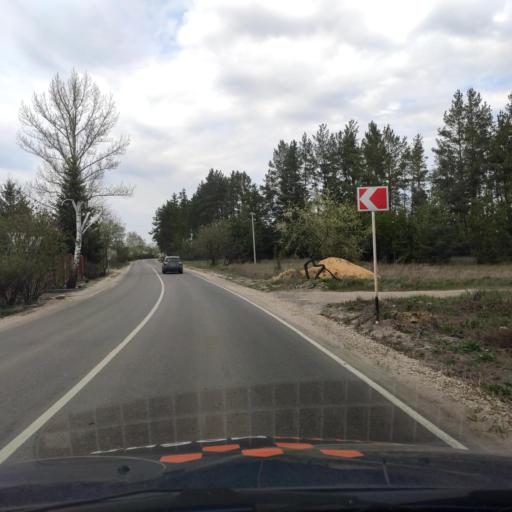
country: RU
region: Voronezj
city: Podgornoye
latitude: 51.8323
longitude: 39.1442
